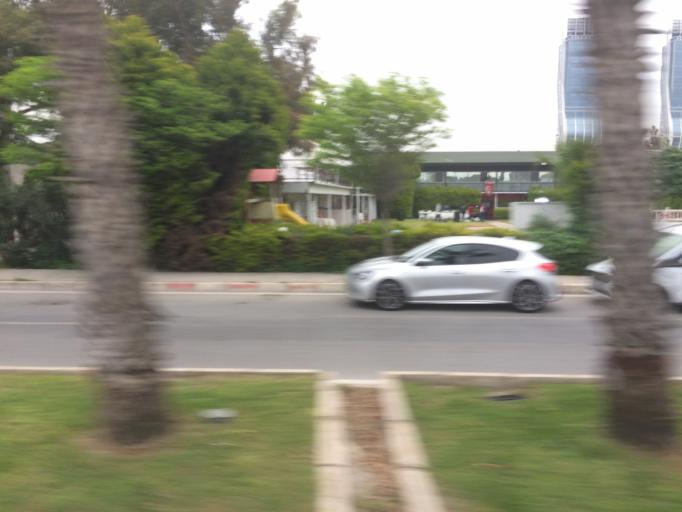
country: TR
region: Izmir
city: Izmir
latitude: 38.4539
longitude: 27.1684
